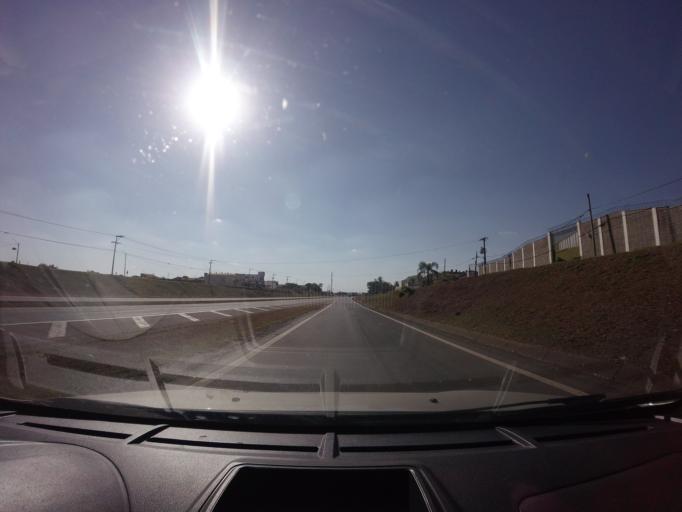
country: BR
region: Sao Paulo
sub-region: Piracicaba
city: Piracicaba
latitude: -22.7635
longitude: -47.5954
